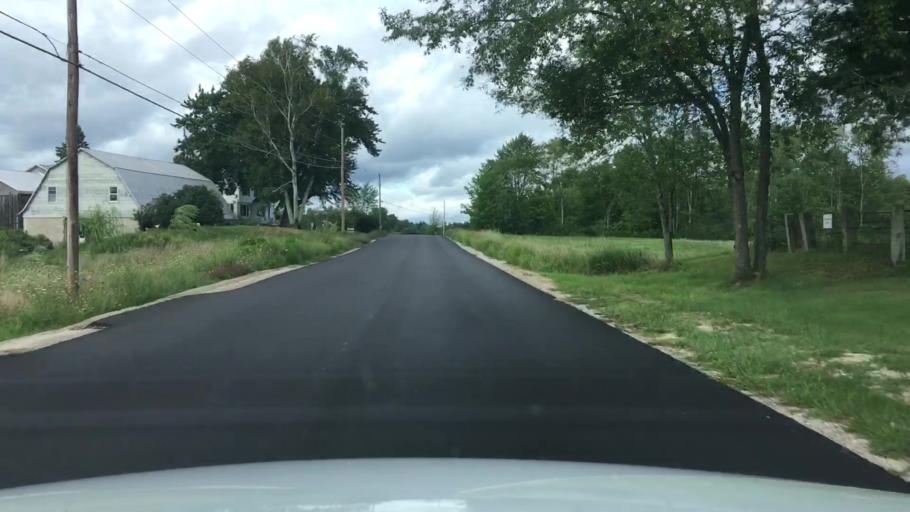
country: US
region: Maine
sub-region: York County
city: West Kennebunk
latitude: 43.4452
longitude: -70.6251
